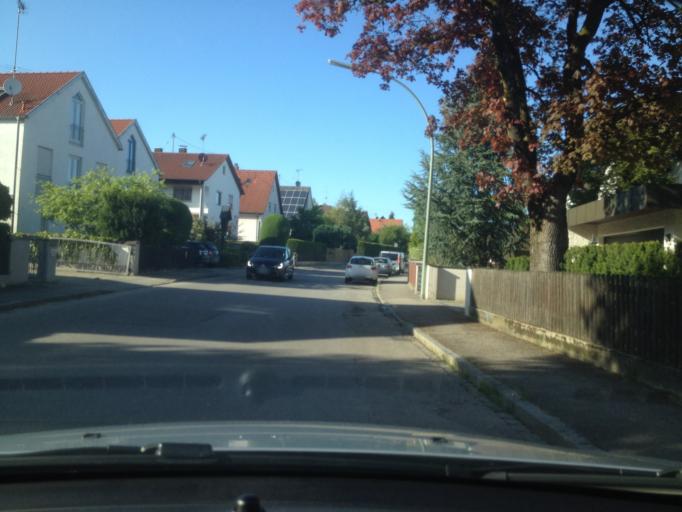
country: DE
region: Bavaria
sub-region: Swabia
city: Diedorf
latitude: 48.3226
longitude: 10.8213
